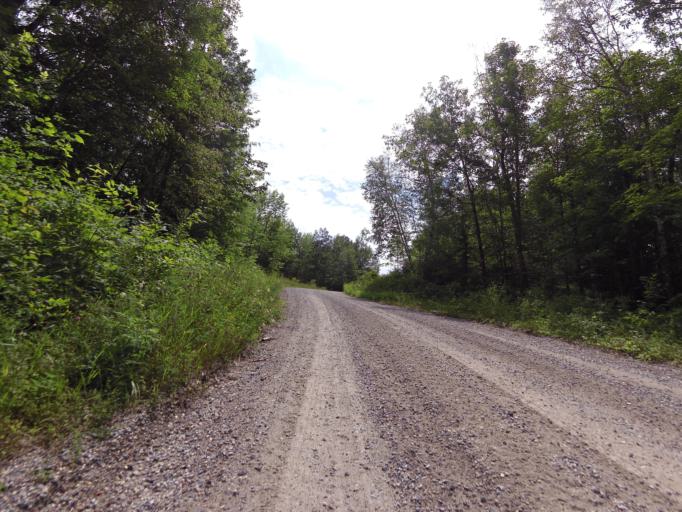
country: CA
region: Ontario
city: Perth
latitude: 44.7460
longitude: -76.6126
